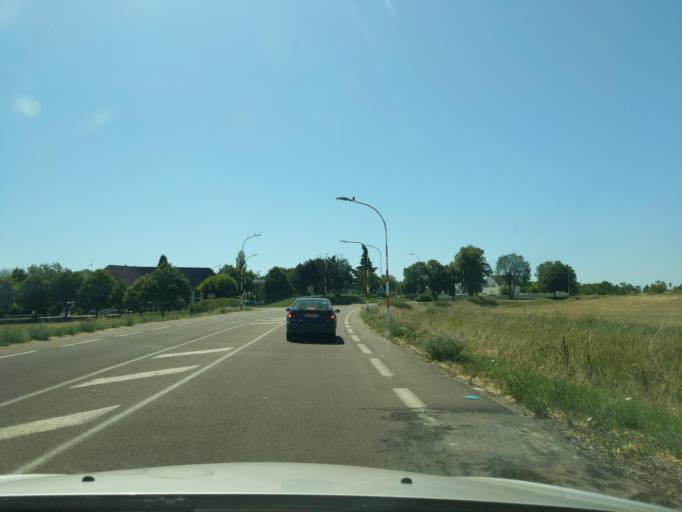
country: FR
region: Bourgogne
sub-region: Departement de la Cote-d'Or
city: Sennecey-les-Dijon
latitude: 47.2894
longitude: 5.0968
